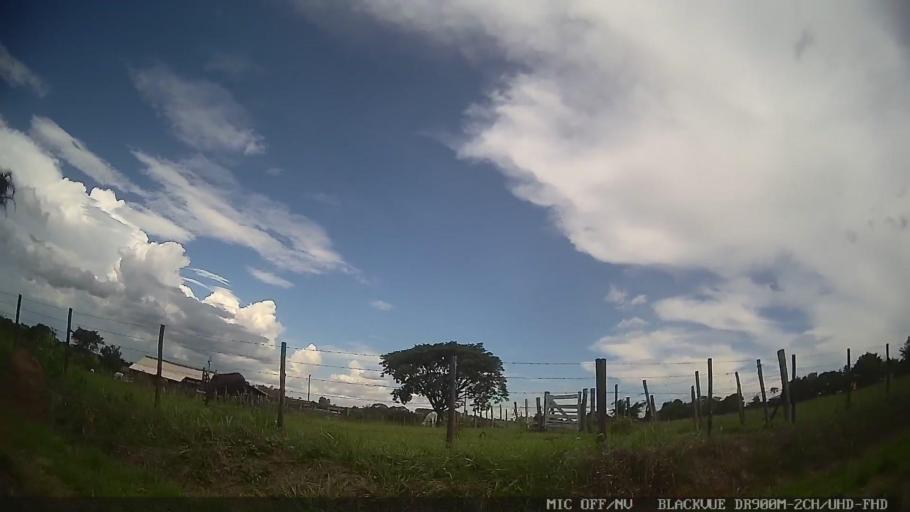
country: BR
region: Sao Paulo
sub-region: Conchas
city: Conchas
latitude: -22.9629
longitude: -47.9819
